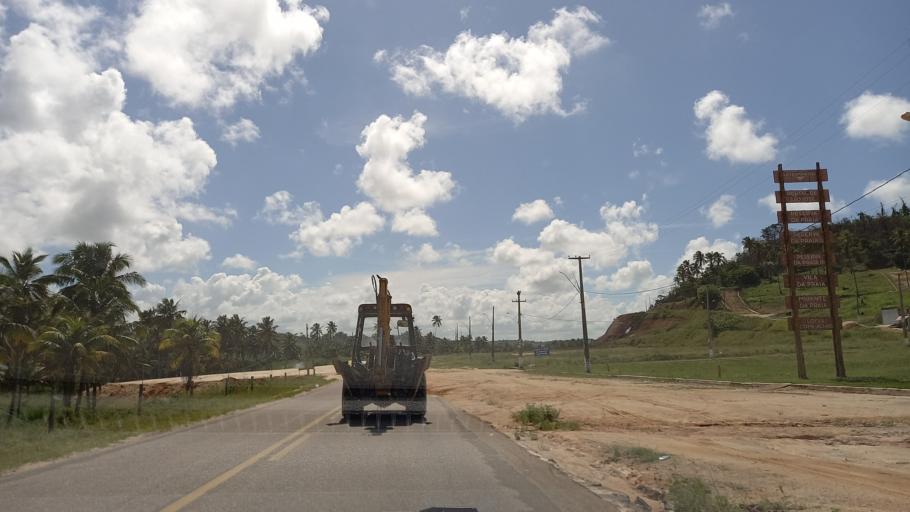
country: BR
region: Pernambuco
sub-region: Sao Jose Da Coroa Grande
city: Sao Jose da Coroa Grande
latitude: -8.8798
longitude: -35.1587
